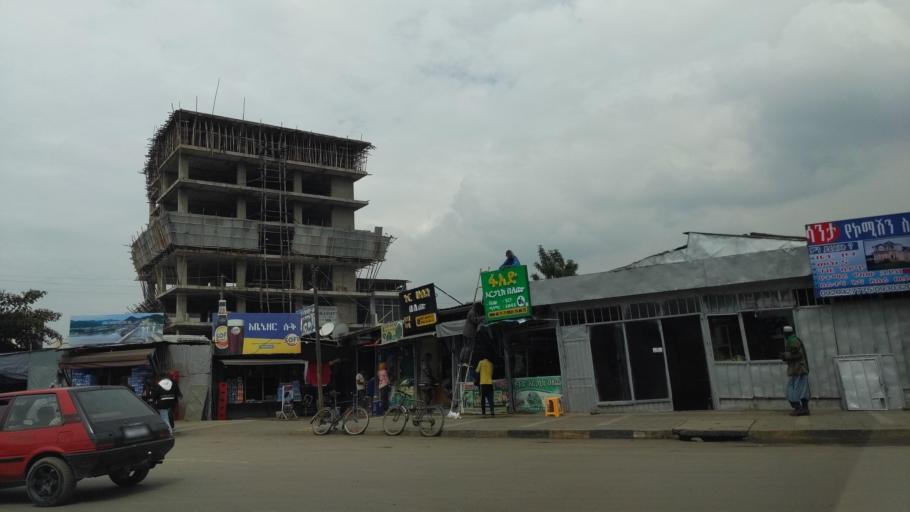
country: ET
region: Adis Abeba
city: Addis Ababa
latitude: 9.0007
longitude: 38.7666
